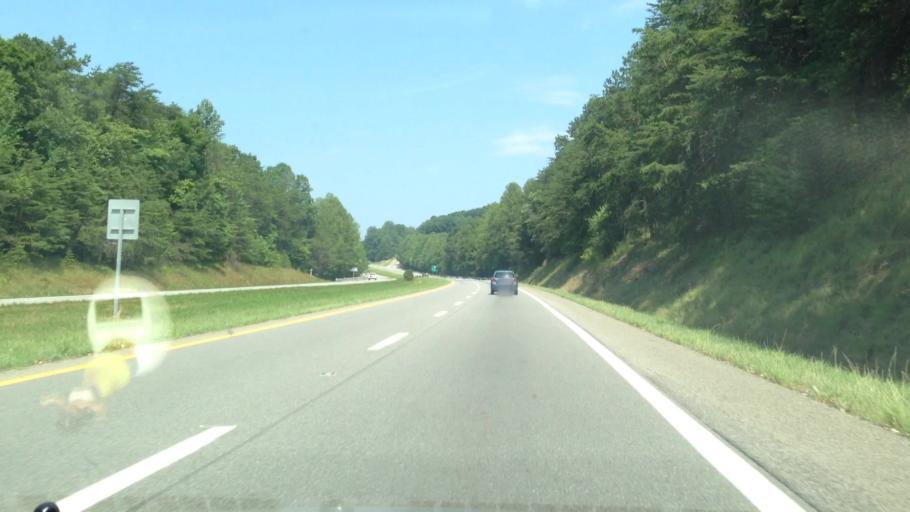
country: US
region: Virginia
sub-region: Henry County
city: Collinsville
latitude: 36.6887
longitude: -79.9430
